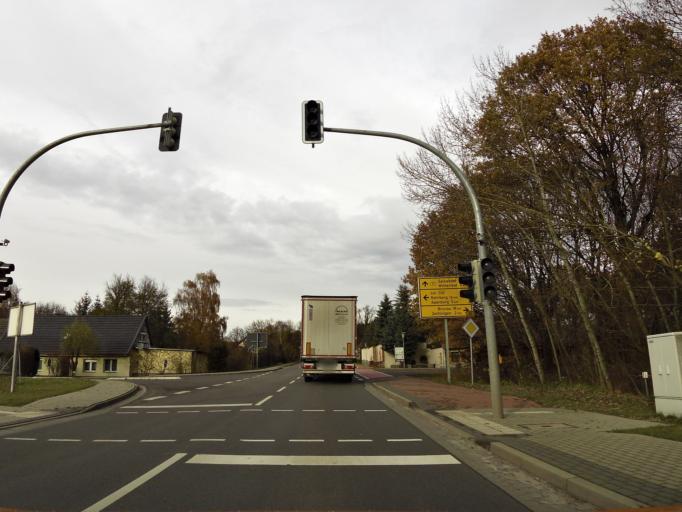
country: DE
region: Saxony-Anhalt
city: Klotze
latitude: 52.7032
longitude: 11.2546
